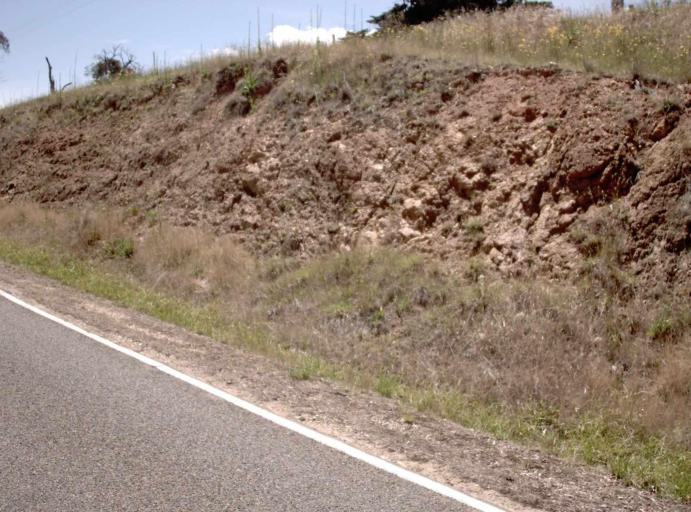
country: AU
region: Victoria
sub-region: Alpine
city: Mount Beauty
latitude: -37.1079
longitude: 147.5798
